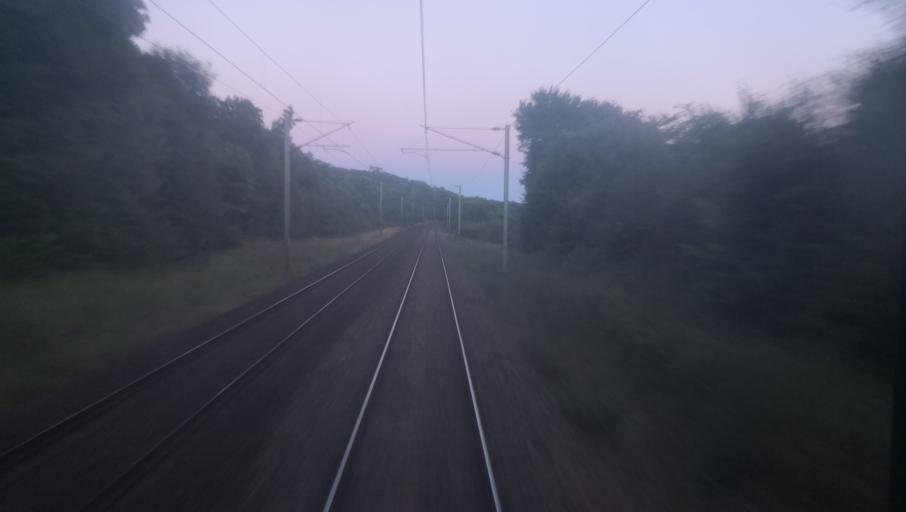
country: FR
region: Centre
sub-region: Departement du Loiret
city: Saint-Brisson-sur-Loire
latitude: 47.6643
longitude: 2.7096
